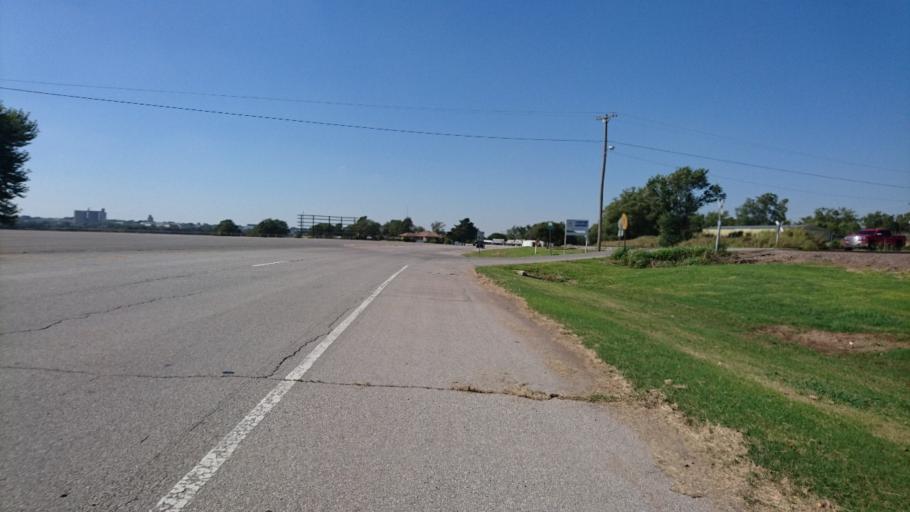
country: US
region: Oklahoma
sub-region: Custer County
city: Clinton
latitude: 35.5143
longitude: -98.9401
